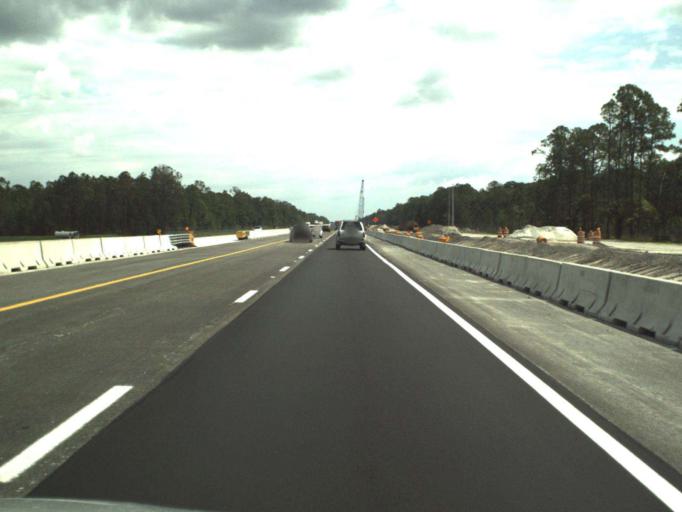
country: US
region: Florida
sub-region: Volusia County
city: Samsula-Spruce Creek
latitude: 29.1047
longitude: -81.1493
